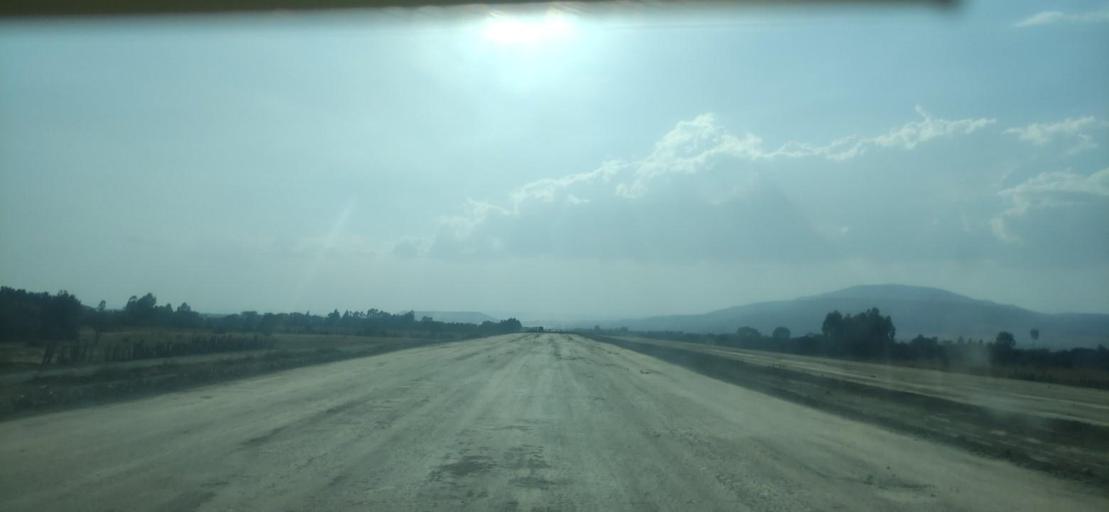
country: ET
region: Oromiya
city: Shashemene
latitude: 7.1884
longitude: 38.5181
